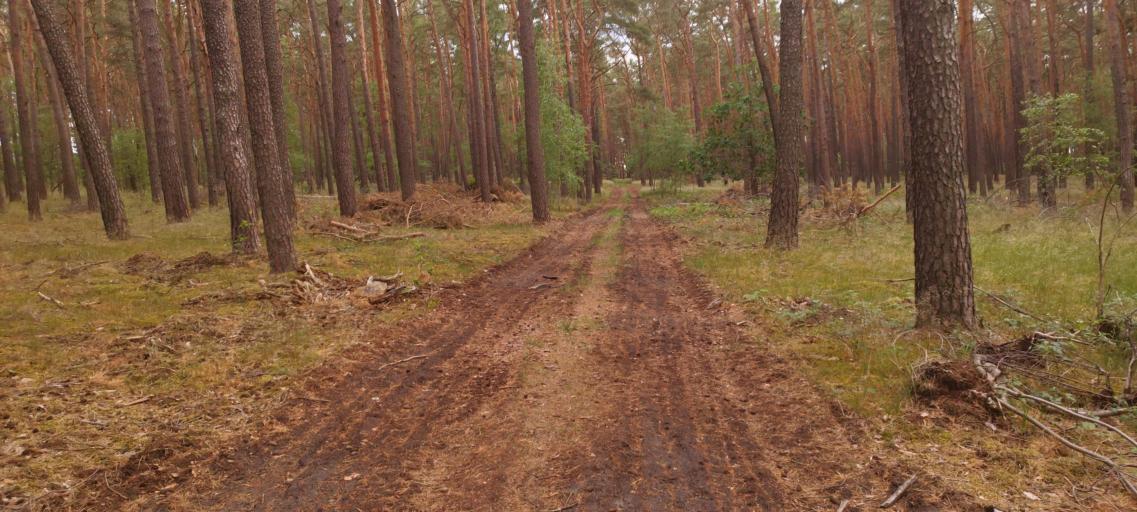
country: DE
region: Berlin
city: Muggelheim
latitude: 52.3972
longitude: 13.6670
